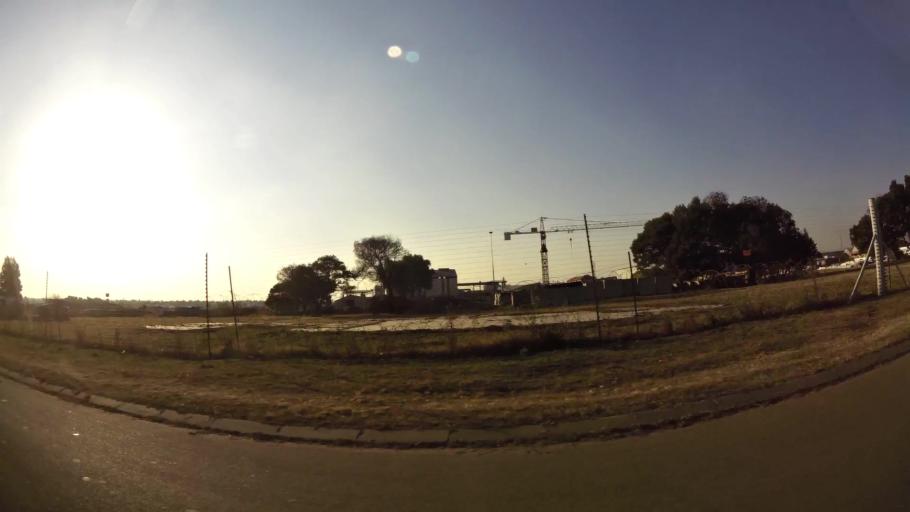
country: ZA
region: Gauteng
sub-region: West Rand District Municipality
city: Randfontein
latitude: -26.2025
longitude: 27.6872
